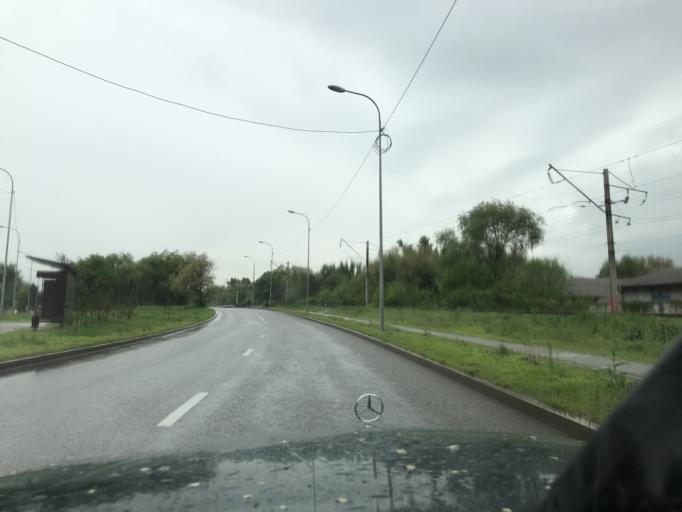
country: KZ
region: Almaty Oblysy
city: Pervomayskiy
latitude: 43.3331
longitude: 76.9602
